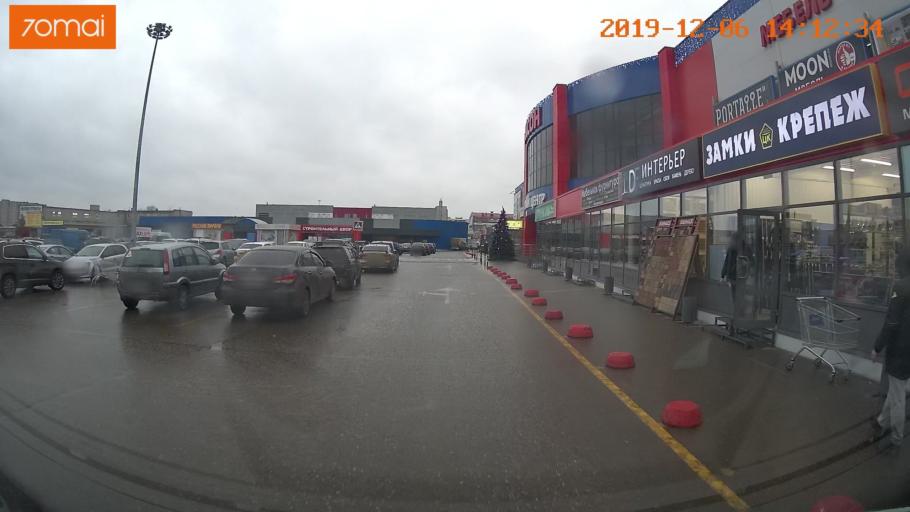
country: RU
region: Ivanovo
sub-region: Gorod Ivanovo
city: Ivanovo
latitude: 56.9595
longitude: 40.9823
